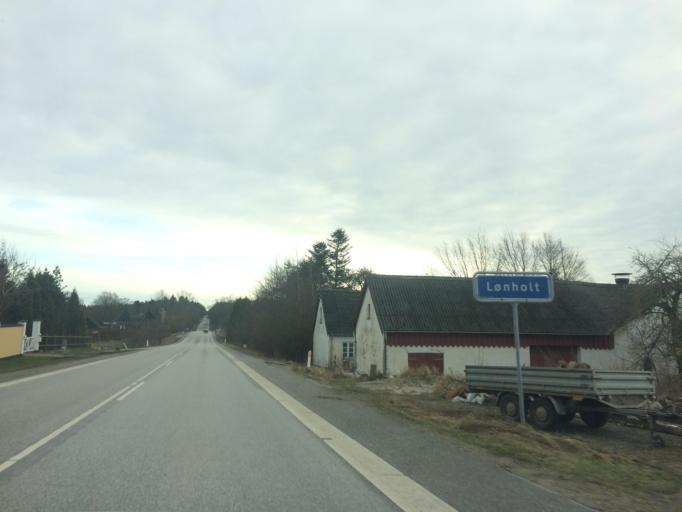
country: DK
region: Capital Region
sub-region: Fredensborg Kommune
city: Fredensborg
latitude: 55.9474
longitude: 12.4232
